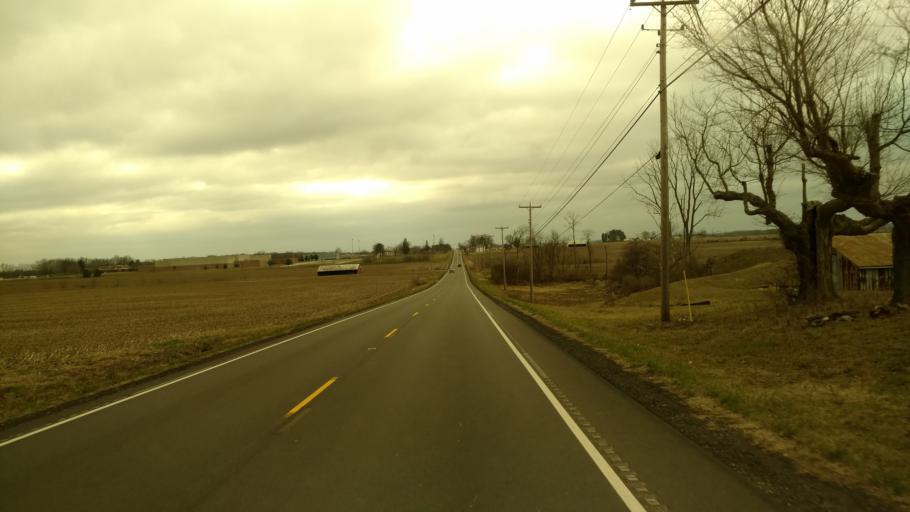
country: US
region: Ohio
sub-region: Licking County
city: Harbor Hills
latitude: 39.9600
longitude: -82.4282
